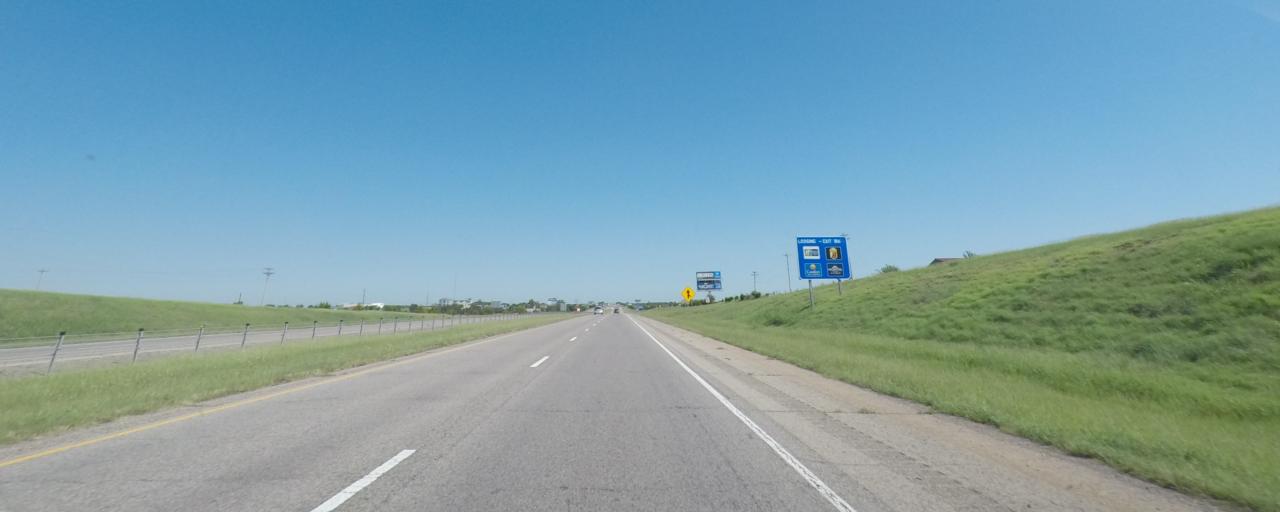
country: US
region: Oklahoma
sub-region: Noble County
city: Perry
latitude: 36.2760
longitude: -97.3276
